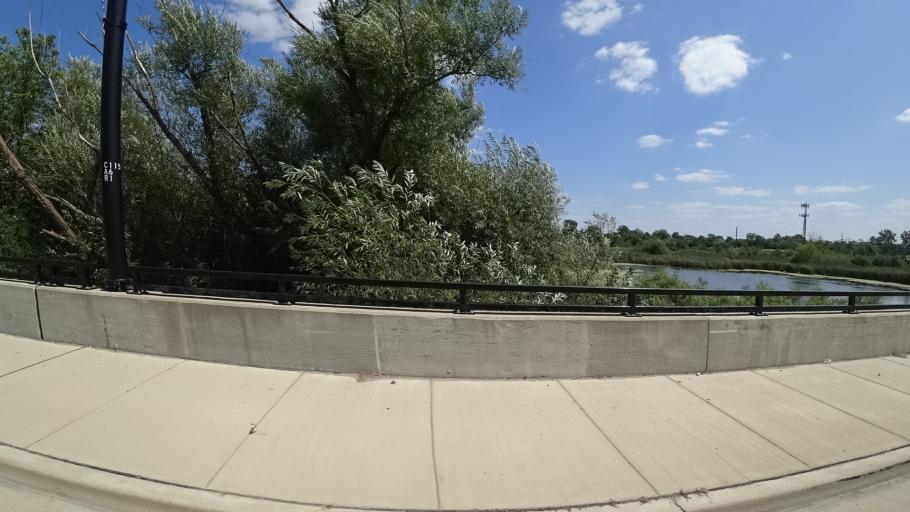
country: US
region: Illinois
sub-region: Cook County
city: Orland Park
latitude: 41.6405
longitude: -87.8536
